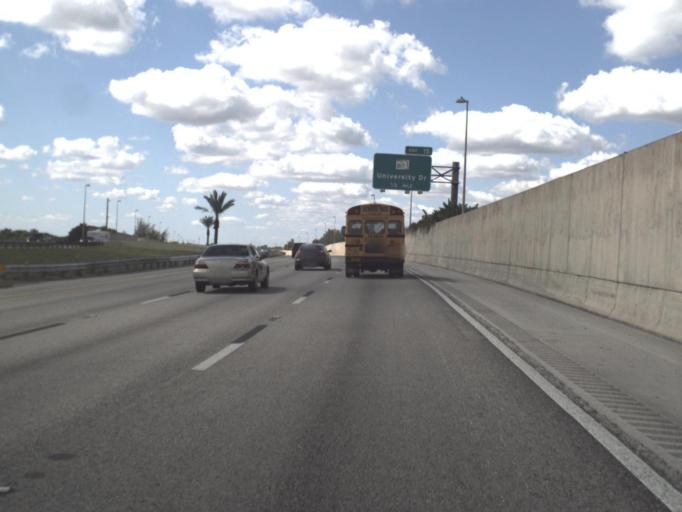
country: US
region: Florida
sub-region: Broward County
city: Parkland
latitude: 26.3017
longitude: -80.2349
